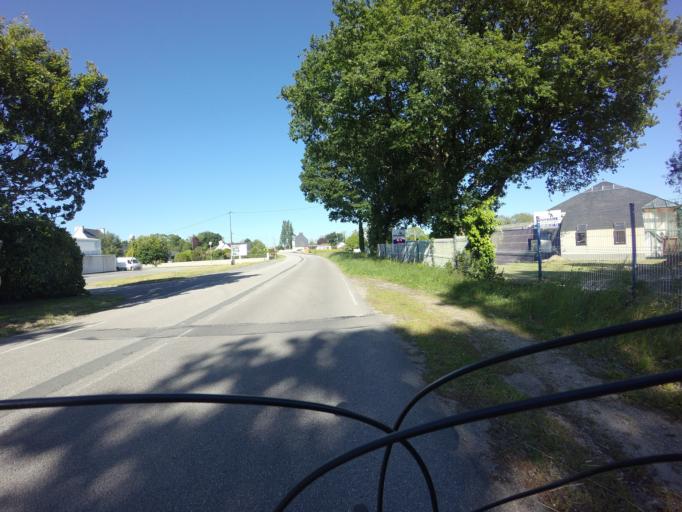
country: FR
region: Brittany
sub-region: Departement du Finistere
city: Plomelin
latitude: 47.9702
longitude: -4.1401
